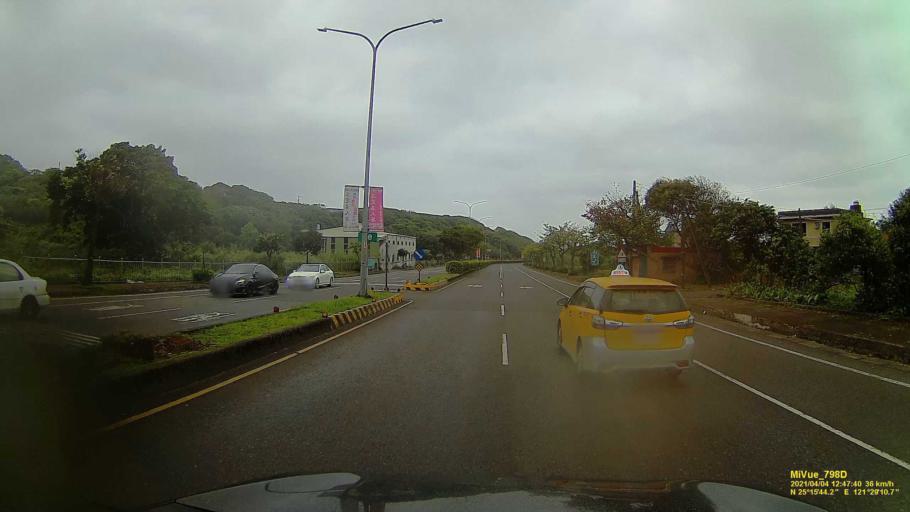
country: TW
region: Taipei
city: Taipei
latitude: 25.2623
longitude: 121.4861
